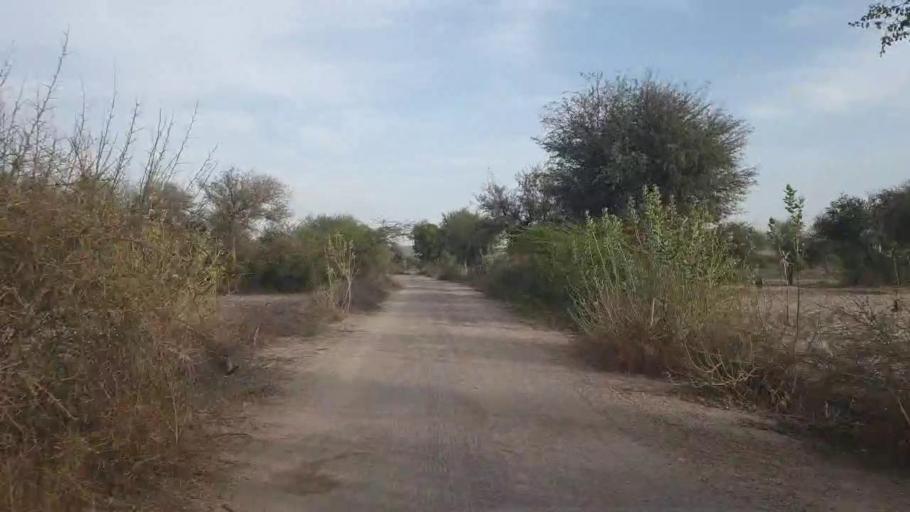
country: PK
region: Sindh
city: Nabisar
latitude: 25.1001
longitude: 69.6678
